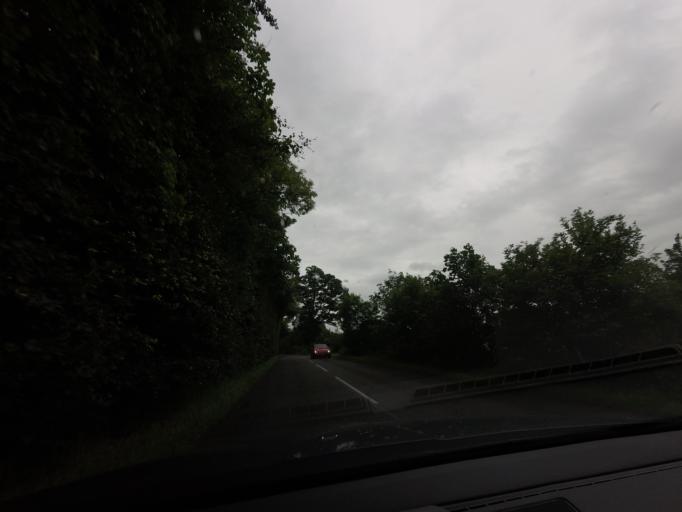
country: GB
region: Scotland
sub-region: Aberdeenshire
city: Turriff
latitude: 57.5396
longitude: -2.4903
